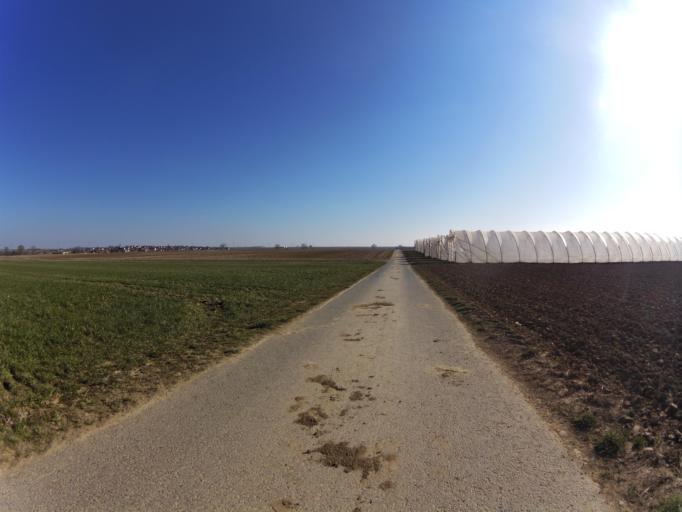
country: DE
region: Bavaria
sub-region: Regierungsbezirk Unterfranken
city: Bergtheim
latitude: 49.8865
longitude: 10.0682
